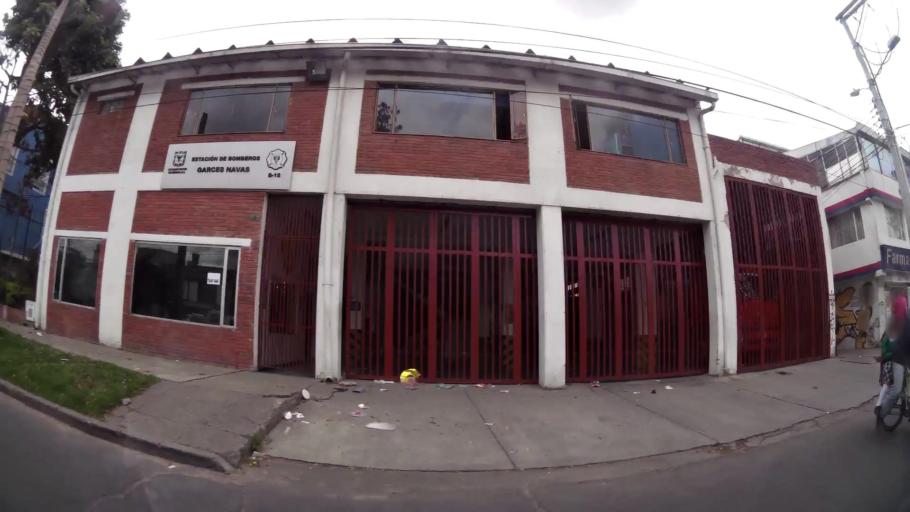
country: CO
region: Cundinamarca
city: Funza
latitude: 4.7143
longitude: -74.1208
